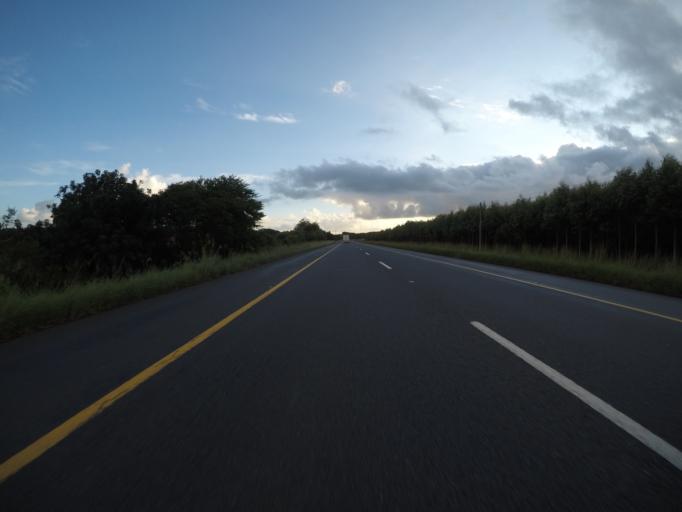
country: ZA
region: KwaZulu-Natal
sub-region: uThungulu District Municipality
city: KwaMbonambi
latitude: -28.5717
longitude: 32.1094
